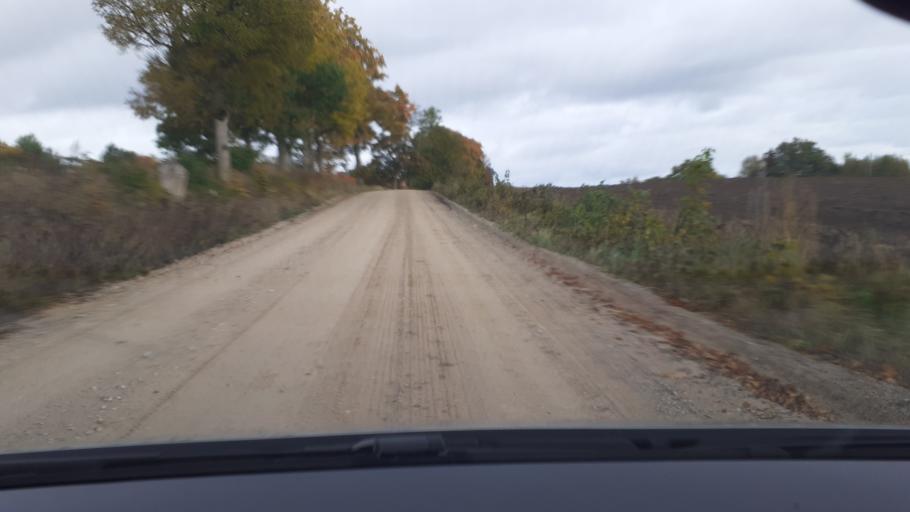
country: LV
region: Kuldigas Rajons
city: Kuldiga
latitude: 57.0213
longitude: 21.9135
